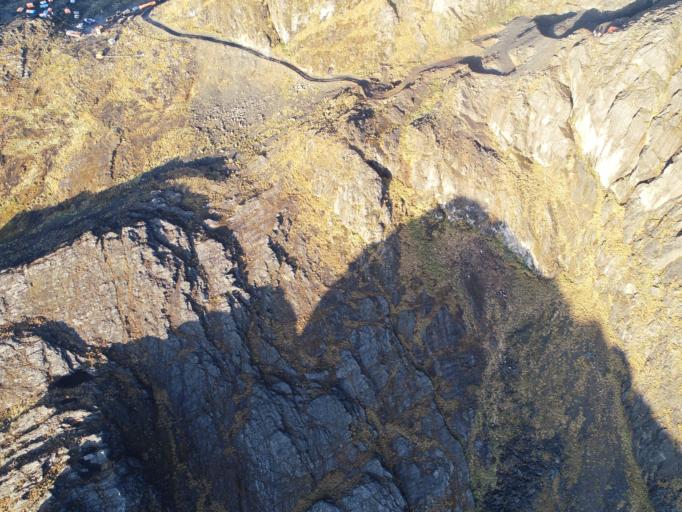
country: PE
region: Puno
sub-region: San Antonio De Putina
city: Sina
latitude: -14.7367
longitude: -69.0474
